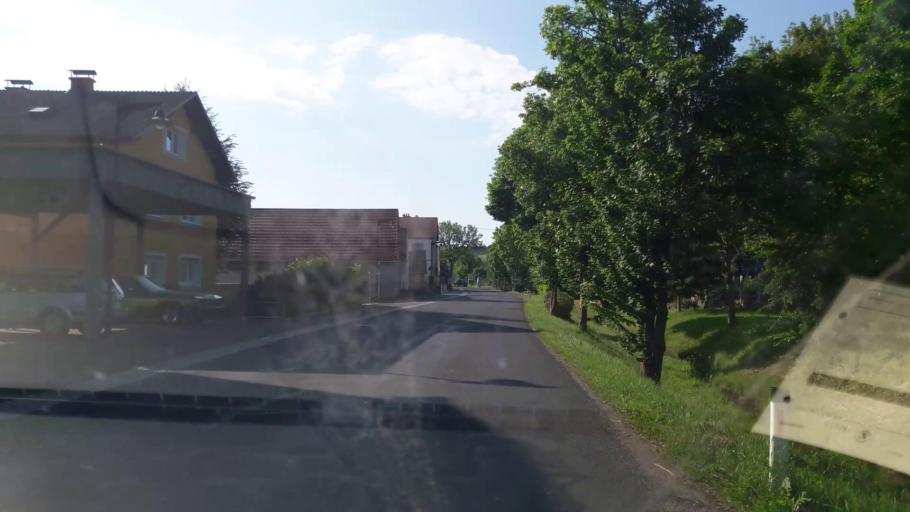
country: AT
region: Styria
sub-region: Politischer Bezirk Suedoststeiermark
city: Unterlamm
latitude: 46.9783
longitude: 16.0580
